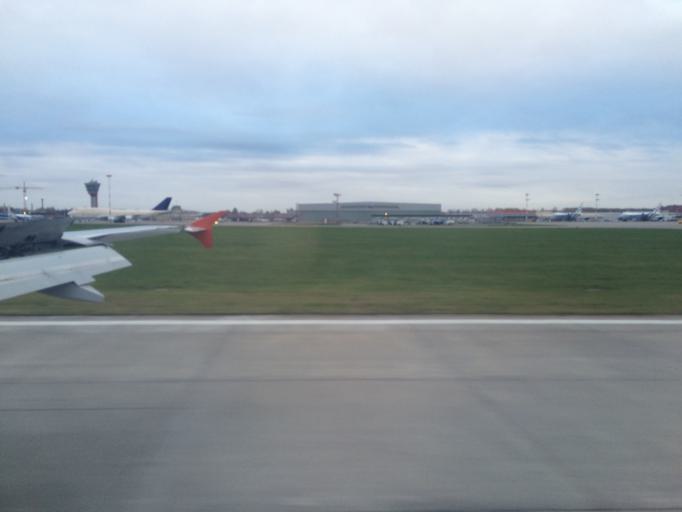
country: RU
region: Moskovskaya
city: Lobnya
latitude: 55.9756
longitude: 37.4262
